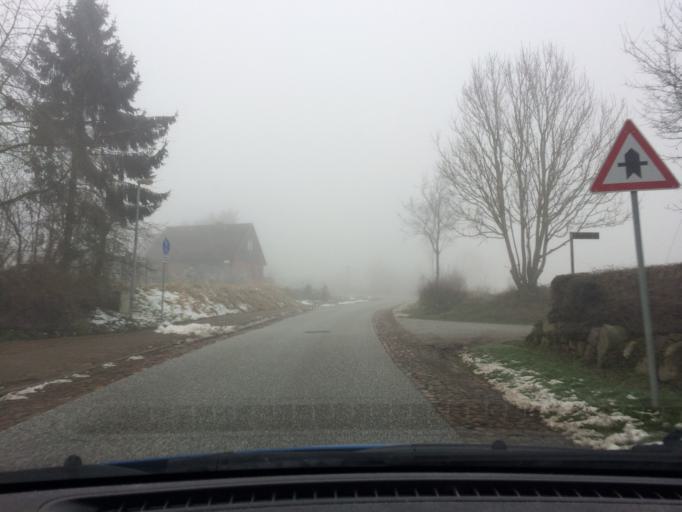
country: DE
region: Schleswig-Holstein
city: Juliusburg
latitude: 53.4179
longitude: 10.5066
